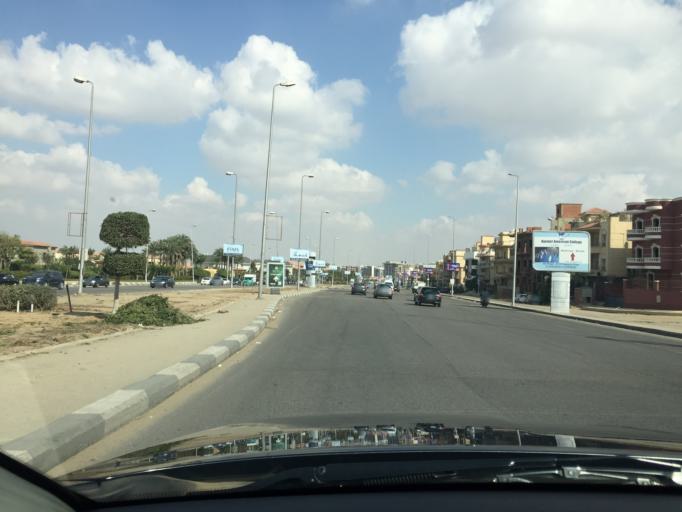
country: EG
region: Muhafazat al Qahirah
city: Cairo
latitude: 30.0203
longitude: 31.4506
